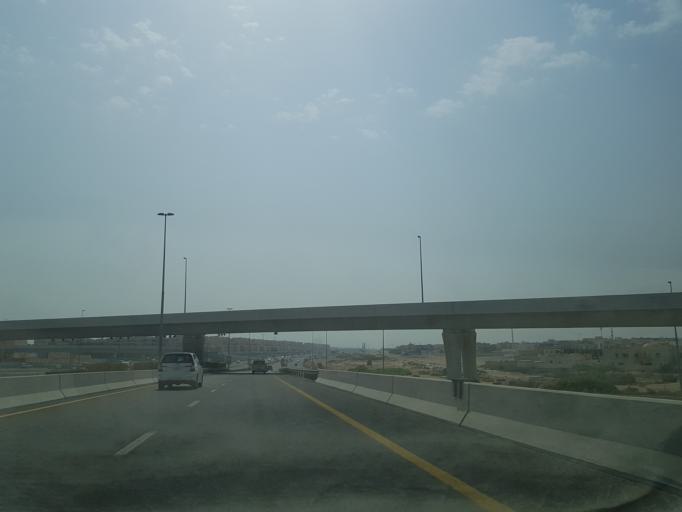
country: AE
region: Ash Shariqah
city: Sharjah
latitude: 25.2121
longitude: 55.4050
